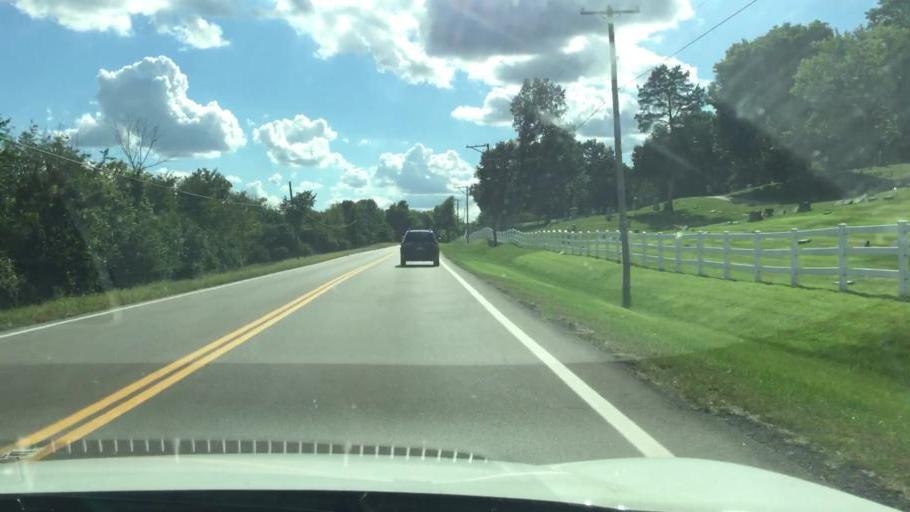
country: US
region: Ohio
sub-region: Clark County
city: Northridge
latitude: 39.9828
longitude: -83.7361
